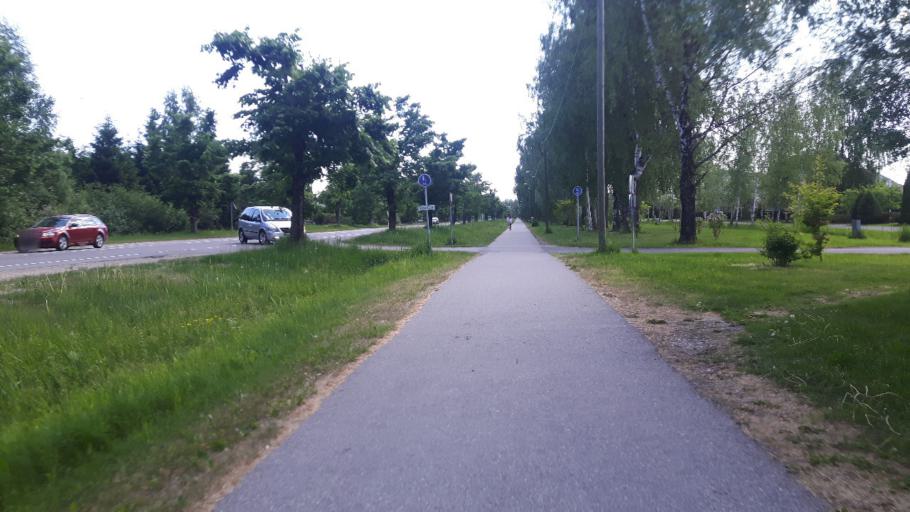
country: EE
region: Paernumaa
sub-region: Paikuse vald
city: Paikuse
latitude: 58.3796
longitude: 24.6289
